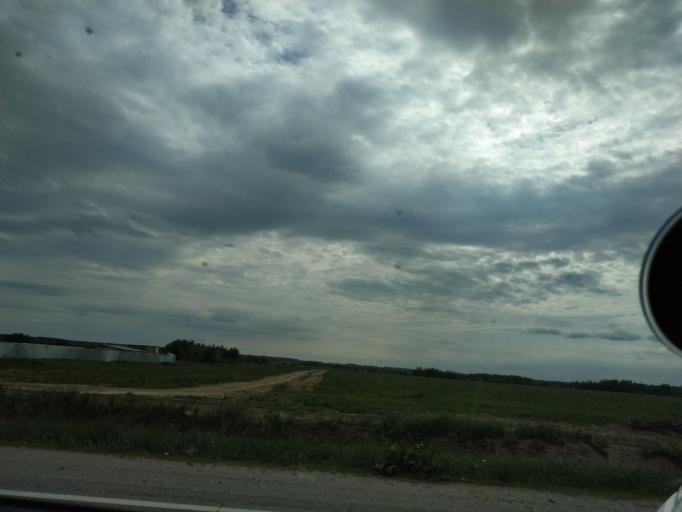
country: RU
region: Moskovskaya
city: Malyshevo
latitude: 55.4980
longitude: 38.3043
